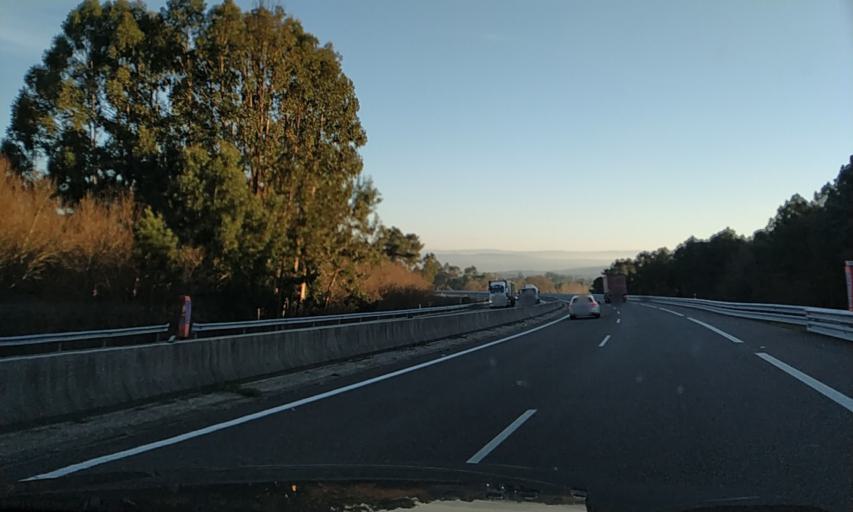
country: ES
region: Galicia
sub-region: Provincia de Ourense
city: Maside
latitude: 42.4375
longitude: -8.0185
